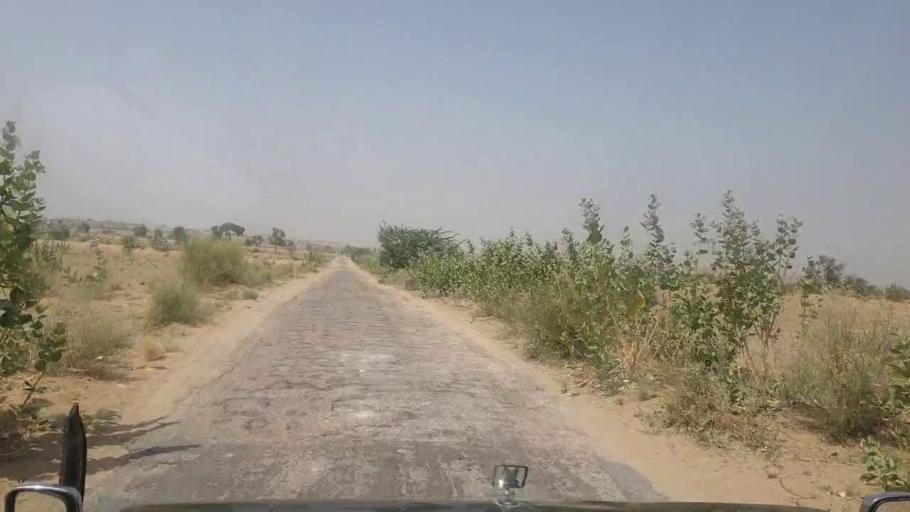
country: PK
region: Sindh
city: Islamkot
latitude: 25.1210
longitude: 70.2317
